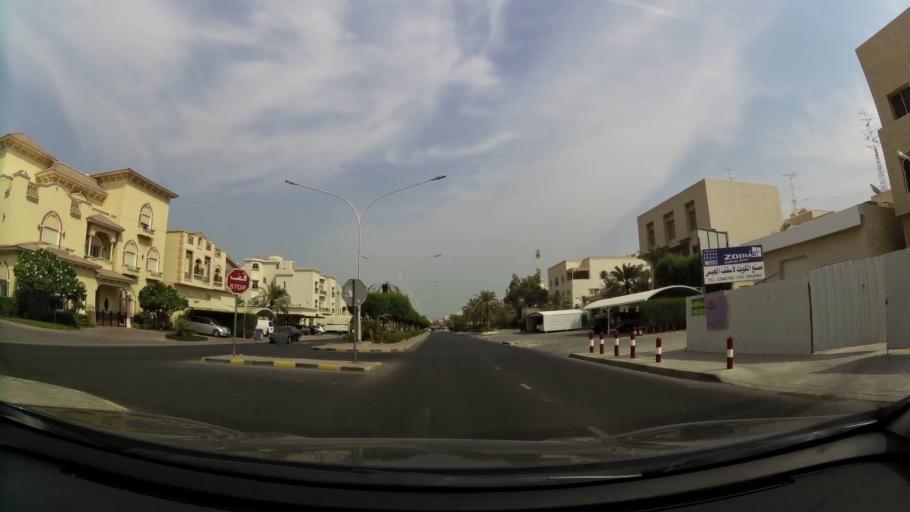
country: KW
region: Al Asimah
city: Ad Dasmah
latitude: 29.3396
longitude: 47.9894
